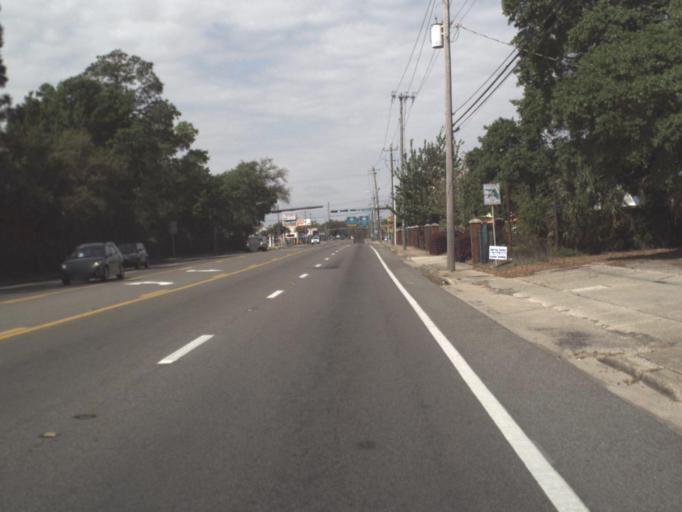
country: US
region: Florida
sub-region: Escambia County
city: Warrington
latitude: 30.3895
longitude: -87.2709
